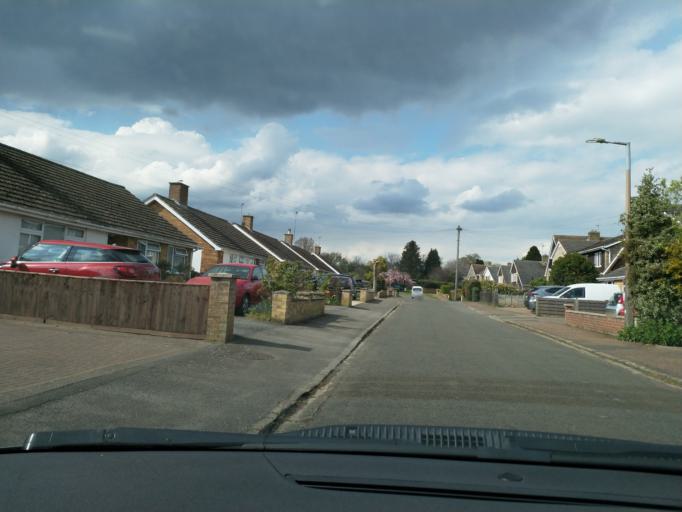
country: GB
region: England
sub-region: Oxfordshire
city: Adderbury
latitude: 52.0228
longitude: -1.3074
